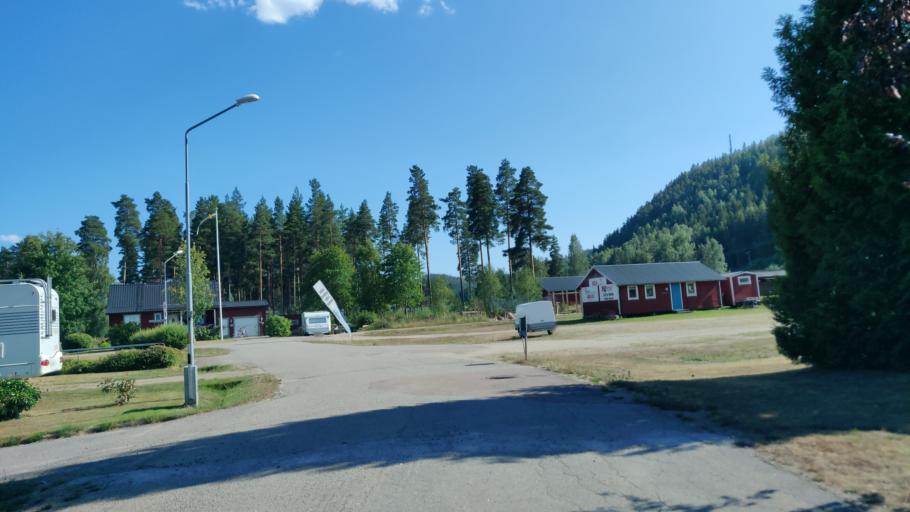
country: SE
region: Vaermland
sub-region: Hagfors Kommun
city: Ekshaerad
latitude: 60.1708
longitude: 13.4925
